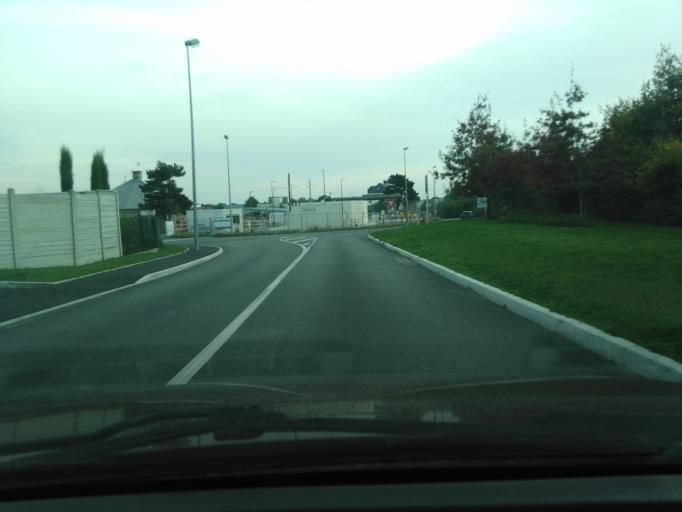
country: FR
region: Pays de la Loire
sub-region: Departement de la Vendee
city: Mouilleron-le-Captif
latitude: 46.7148
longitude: -1.4315
